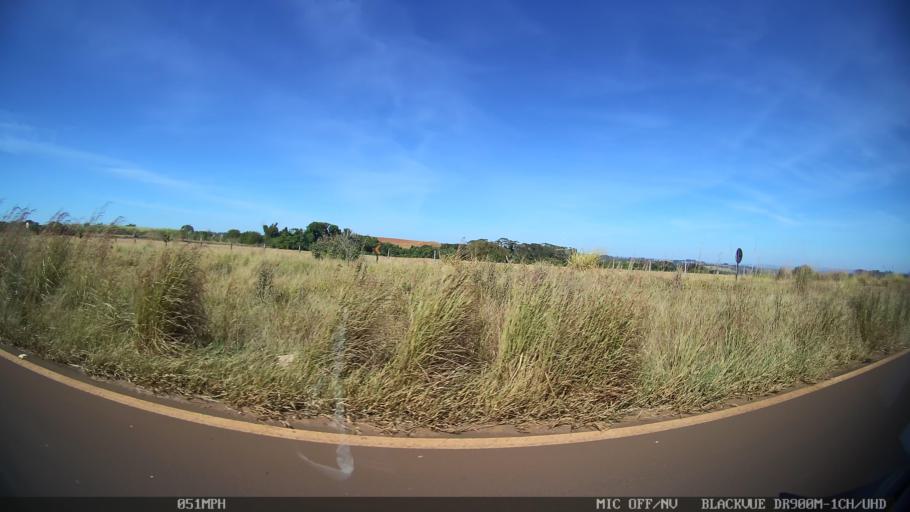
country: BR
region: Sao Paulo
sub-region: Franca
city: Franca
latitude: -20.5478
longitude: -47.4802
